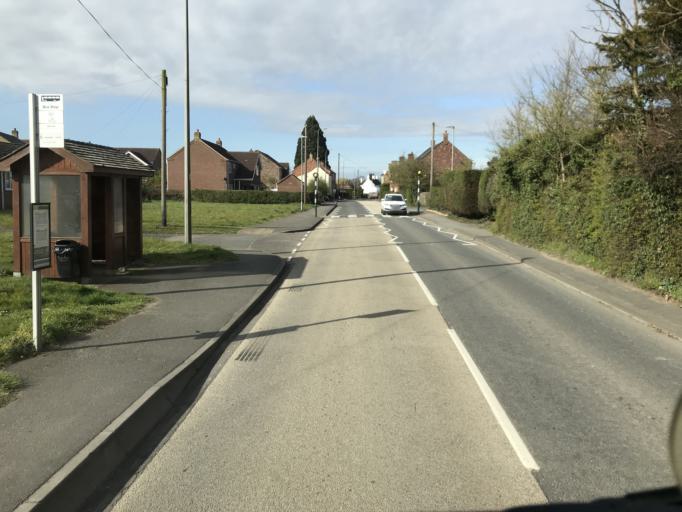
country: GB
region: England
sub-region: Lincolnshire
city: Market Rasen
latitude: 53.3871
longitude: -0.3624
